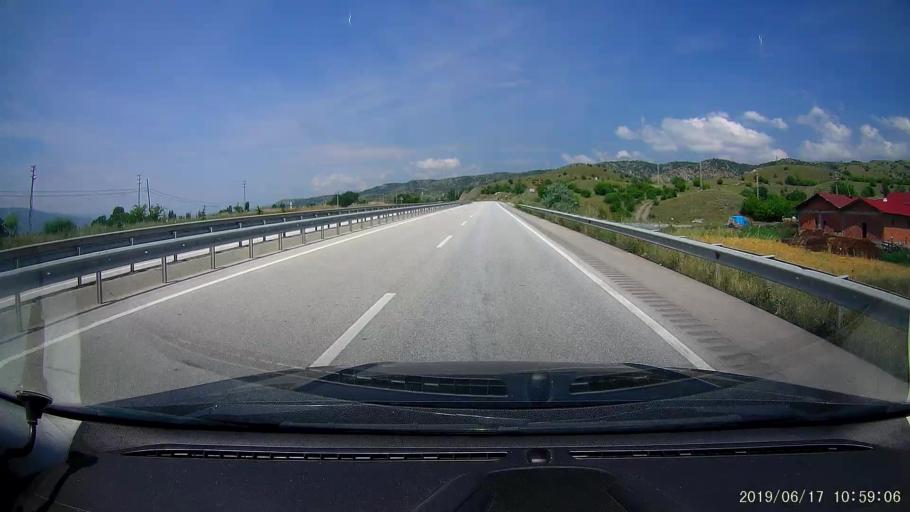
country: TR
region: Kastamonu
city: Tosya
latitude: 41.0407
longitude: 34.2087
